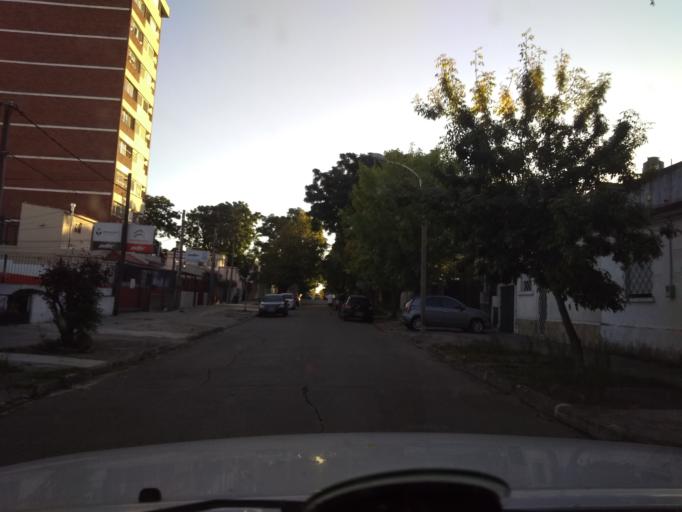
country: UY
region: Montevideo
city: Montevideo
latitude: -34.8904
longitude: -56.1379
